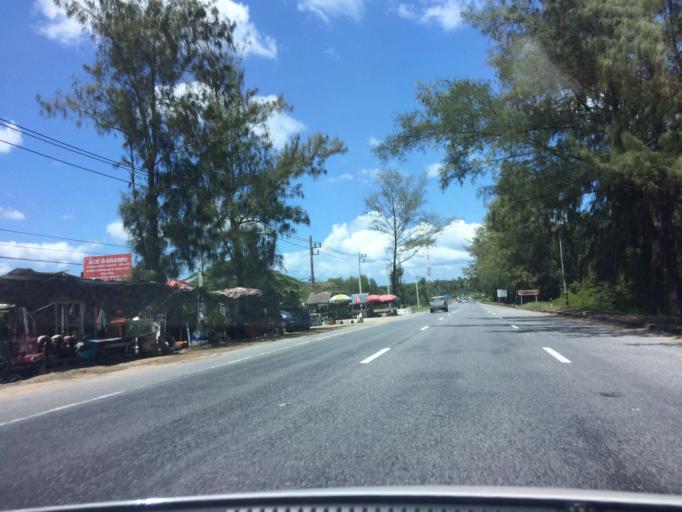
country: TH
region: Phuket
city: Thalang
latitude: 8.2092
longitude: 98.2989
